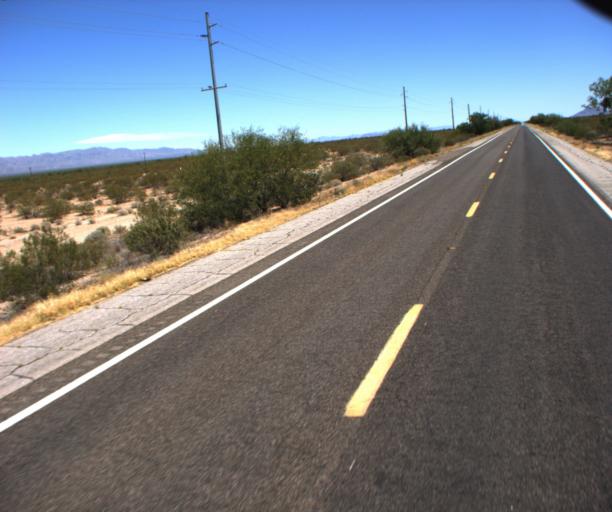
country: US
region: Arizona
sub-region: La Paz County
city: Salome
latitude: 33.8282
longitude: -113.5143
